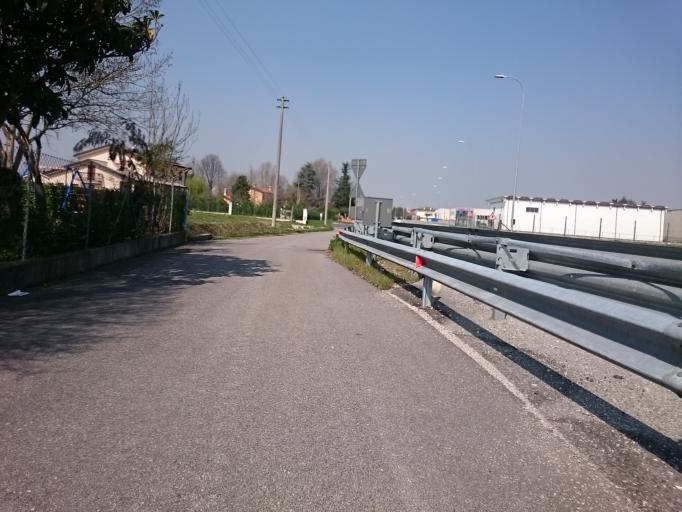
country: IT
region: Veneto
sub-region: Provincia di Padova
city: Sant'Elena
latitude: 45.1861
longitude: 11.7046
